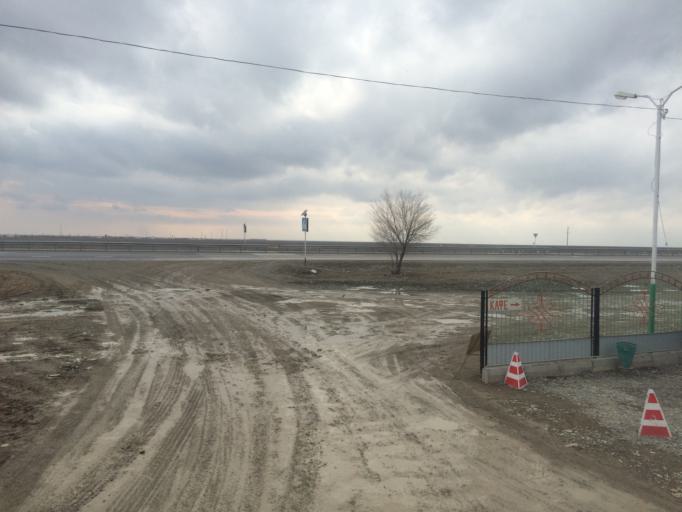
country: KZ
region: Qyzylorda
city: Shalqiya
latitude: 43.6059
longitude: 67.6725
